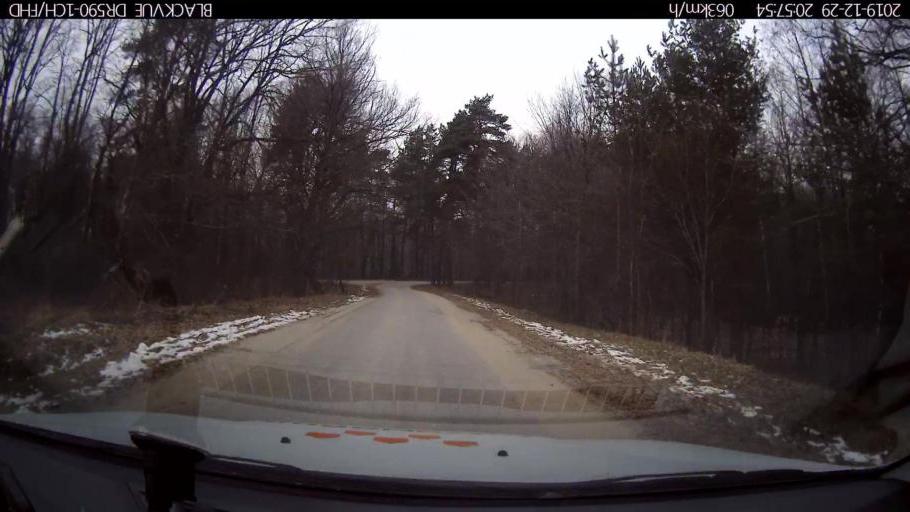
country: RU
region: Nizjnij Novgorod
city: Afonino
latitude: 56.1650
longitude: 43.9887
